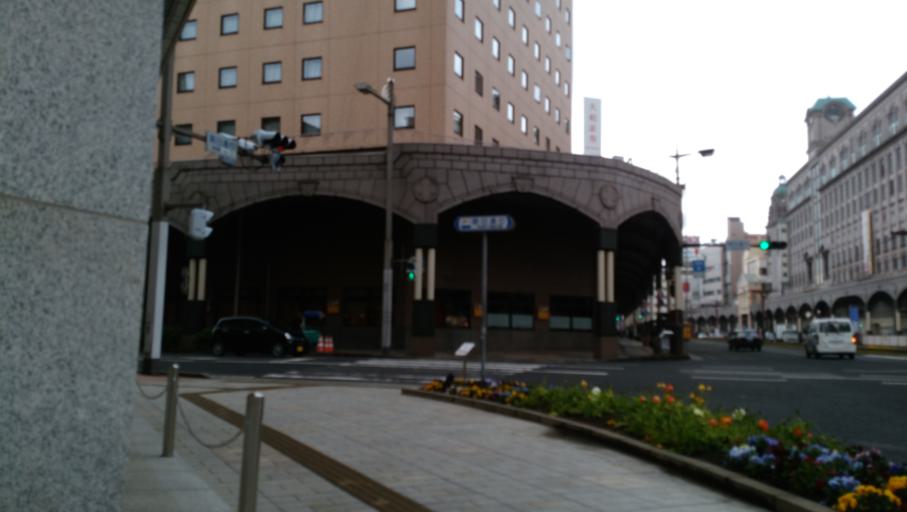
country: JP
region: Kagoshima
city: Kagoshima-shi
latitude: 31.5946
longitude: 130.5574
